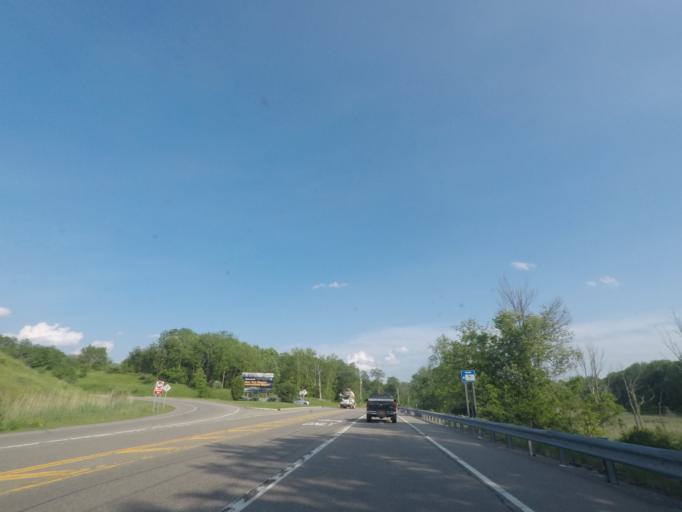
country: US
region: New York
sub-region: Orange County
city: Orange Lake
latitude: 41.4964
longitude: -74.1337
